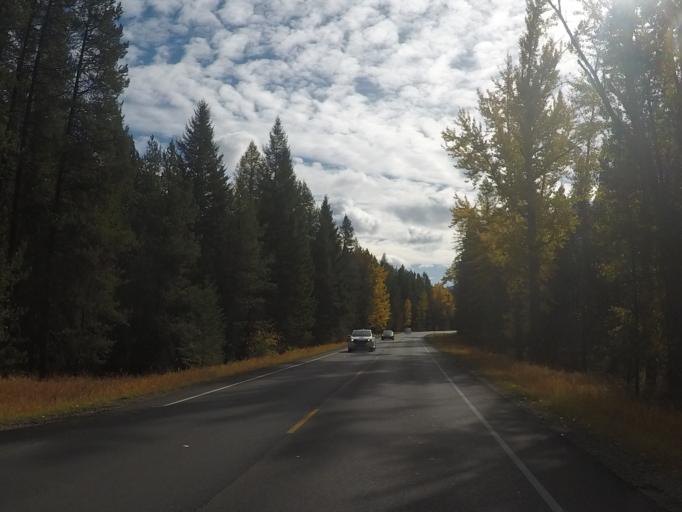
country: US
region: Montana
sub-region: Flathead County
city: Columbia Falls
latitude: 48.5128
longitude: -113.9874
